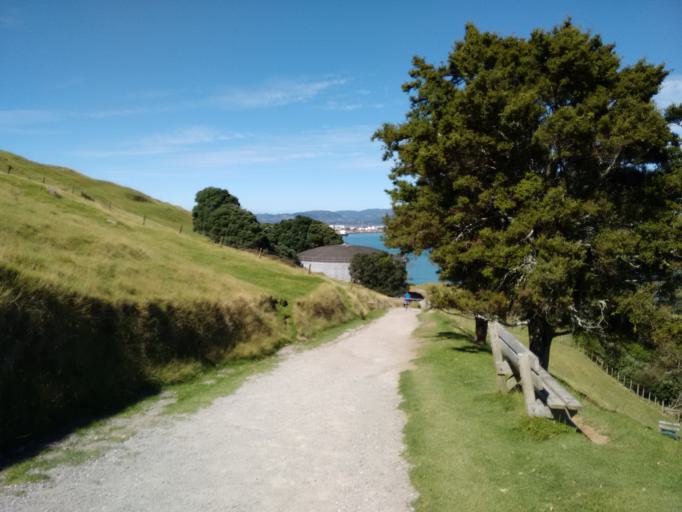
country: NZ
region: Bay of Plenty
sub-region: Tauranga City
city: Tauranga
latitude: -37.6328
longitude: 176.1694
